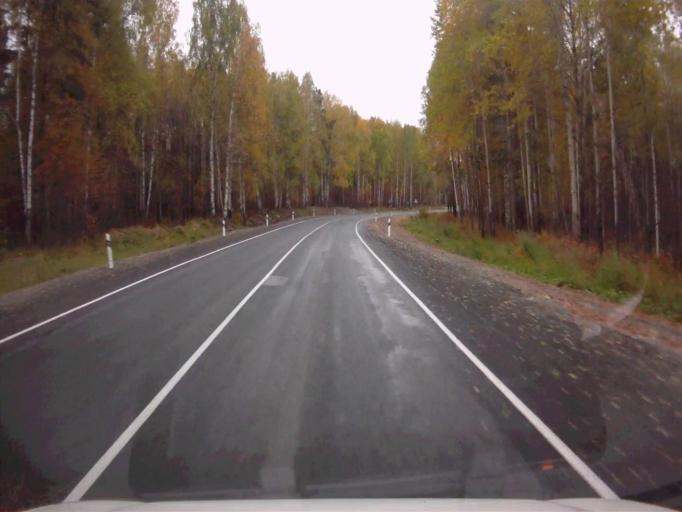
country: RU
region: Chelyabinsk
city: Nyazepetrovsk
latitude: 56.0609
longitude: 59.7300
